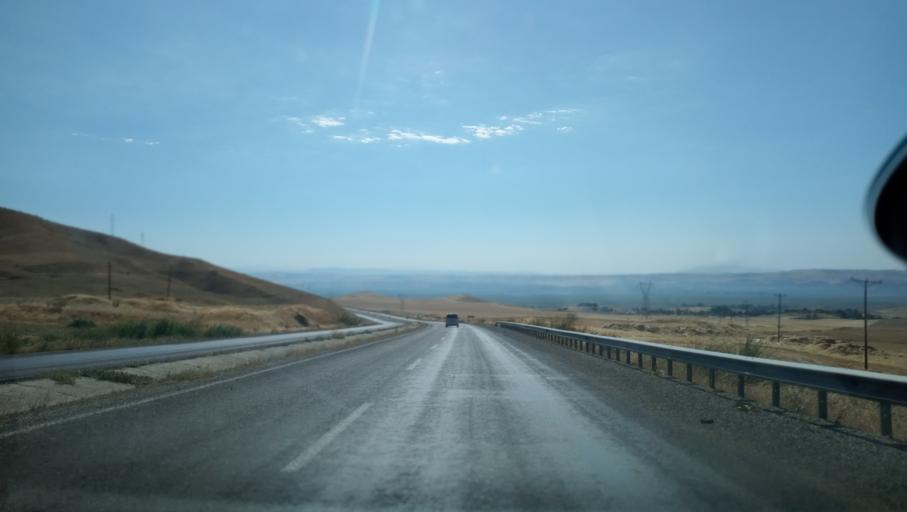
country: TR
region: Diyarbakir
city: Malabadi
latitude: 38.1183
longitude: 41.1355
